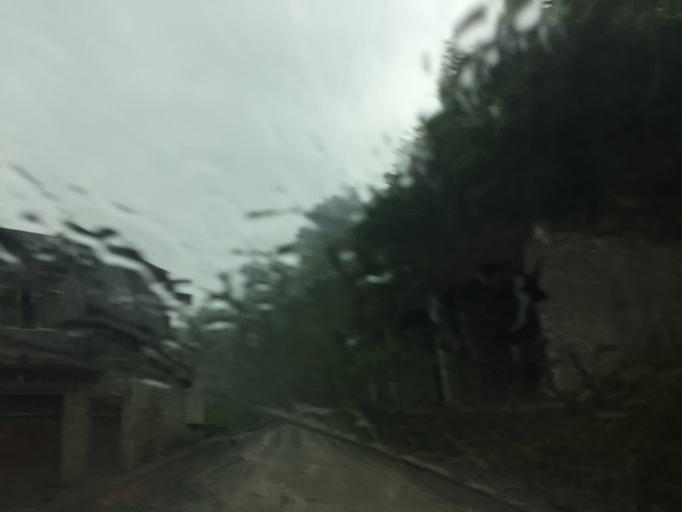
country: CN
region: Guizhou Sheng
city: Changfeng
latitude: 28.4323
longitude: 108.0791
